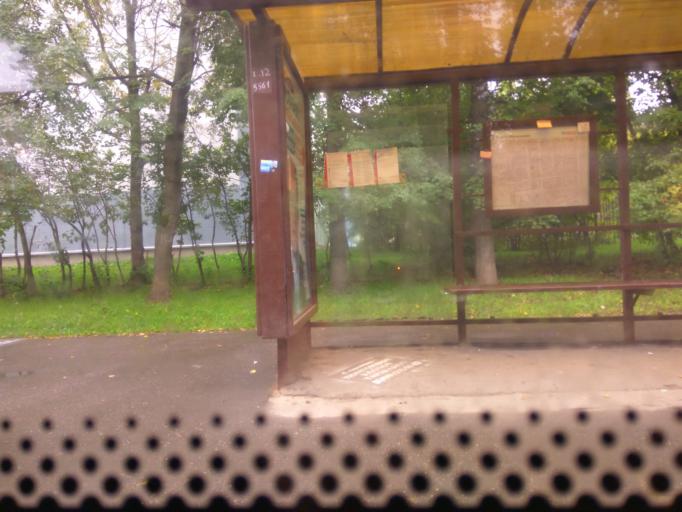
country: RU
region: Moskovskaya
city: Bogorodskoye
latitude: 55.7864
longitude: 37.7309
